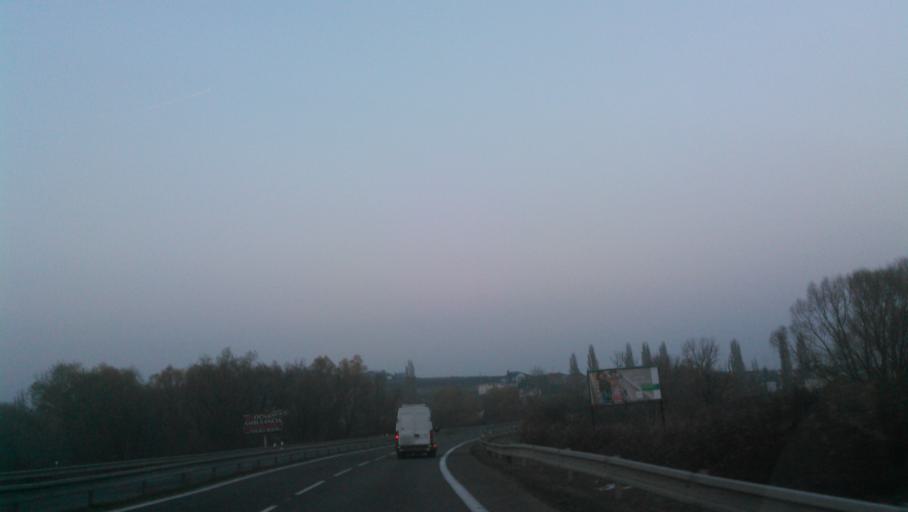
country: SK
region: Bratislavsky
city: Svaty Jur
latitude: 48.2649
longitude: 17.2359
